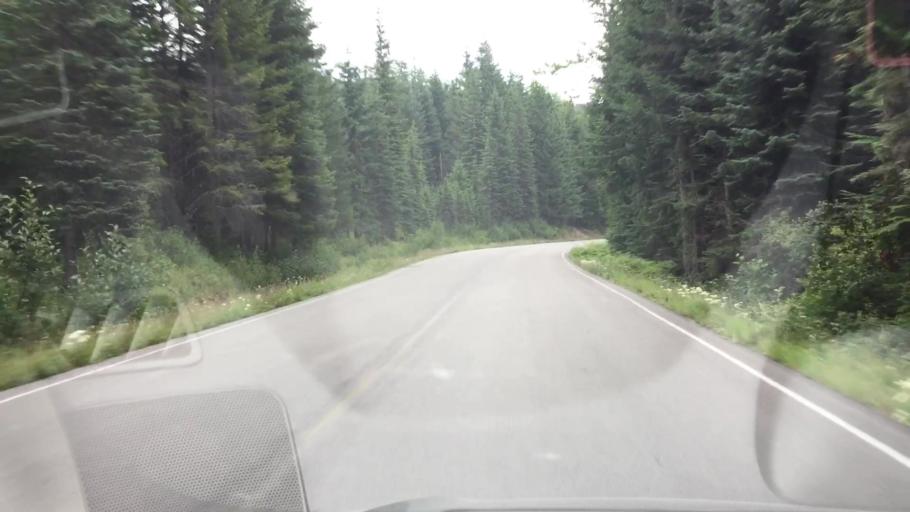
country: US
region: Washington
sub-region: Klickitat County
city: White Salmon
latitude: 46.1795
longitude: -121.6344
